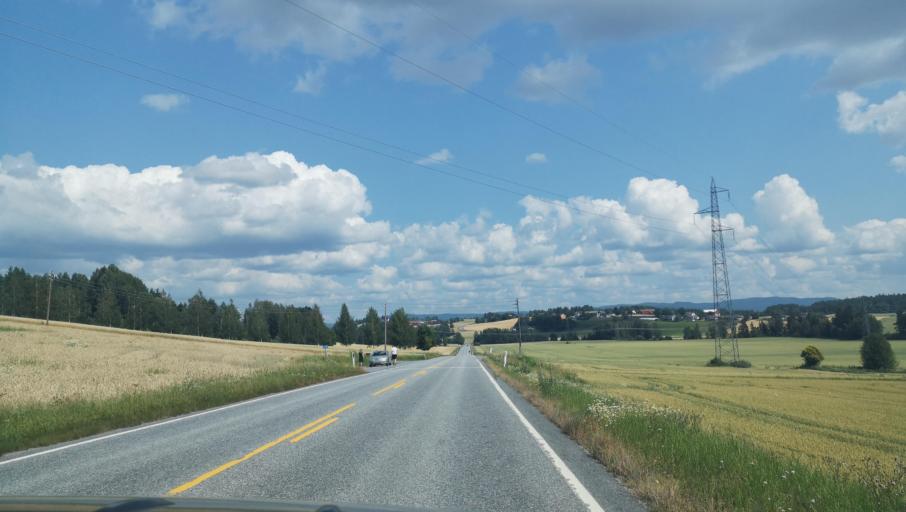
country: NO
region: Buskerud
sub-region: Ovre Eiker
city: Hokksund
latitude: 59.7179
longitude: 9.8236
